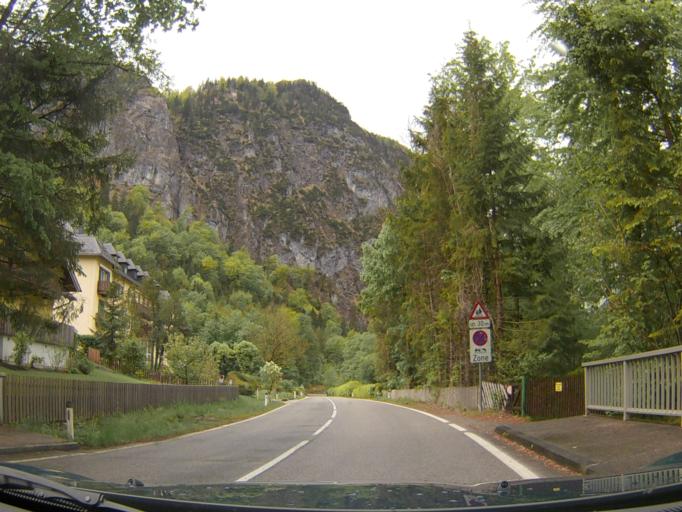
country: AT
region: Upper Austria
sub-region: Politischer Bezirk Vocklabruck
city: Innerschwand
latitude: 47.8006
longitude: 13.4255
